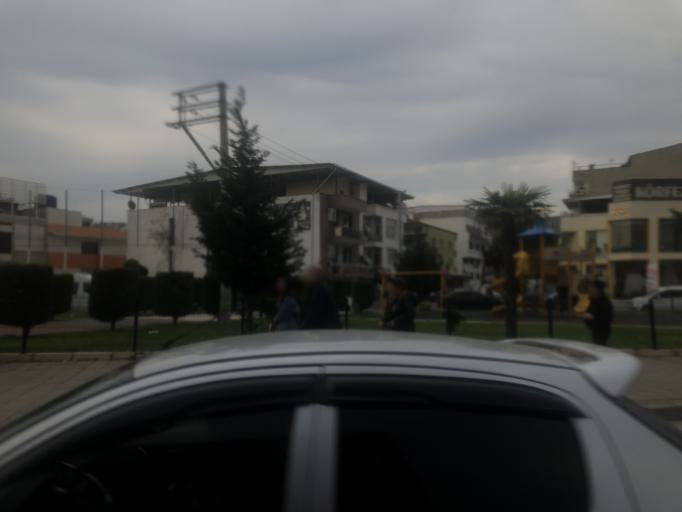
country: TR
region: Izmir
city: Karsiyaka
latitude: 38.4878
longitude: 27.0741
